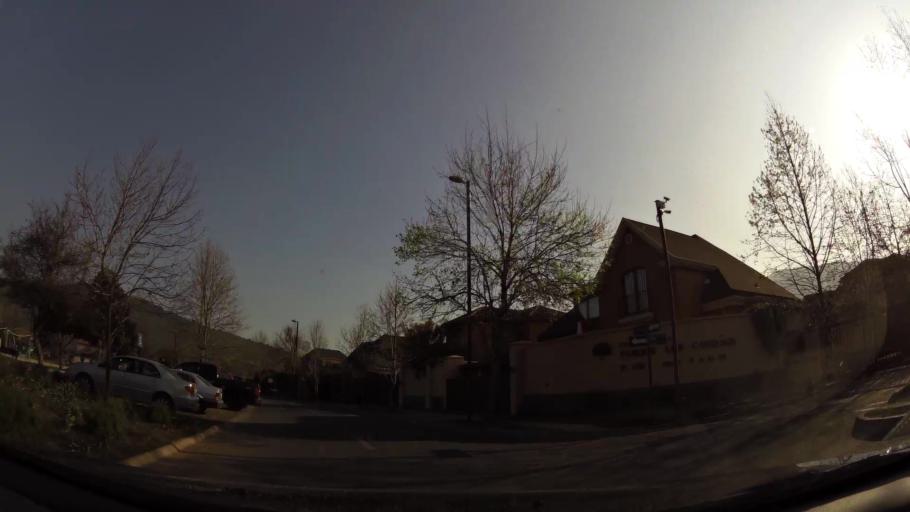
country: CL
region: Santiago Metropolitan
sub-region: Provincia de Santiago
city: Villa Presidente Frei, Nunoa, Santiago, Chile
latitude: -33.3576
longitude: -70.5364
